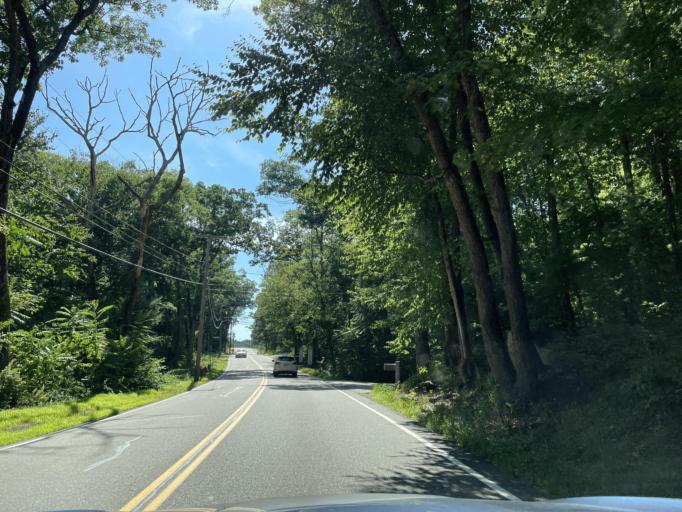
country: US
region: Massachusetts
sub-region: Worcester County
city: Sutton
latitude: 42.1511
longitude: -71.7150
